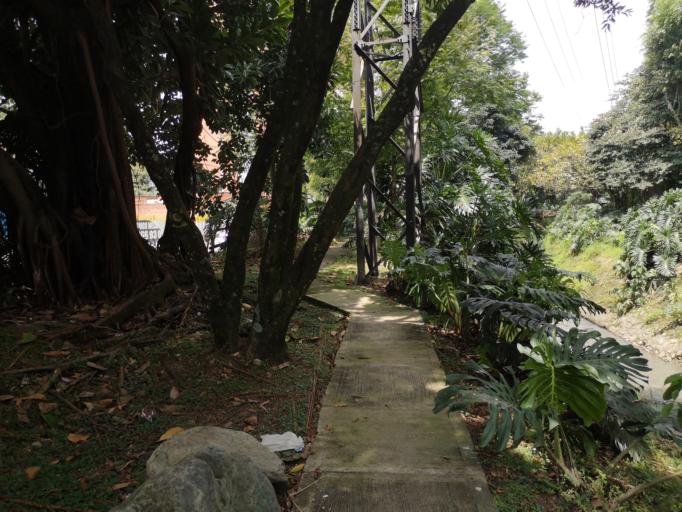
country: CO
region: Antioquia
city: Itagui
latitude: 6.2101
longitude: -75.5758
